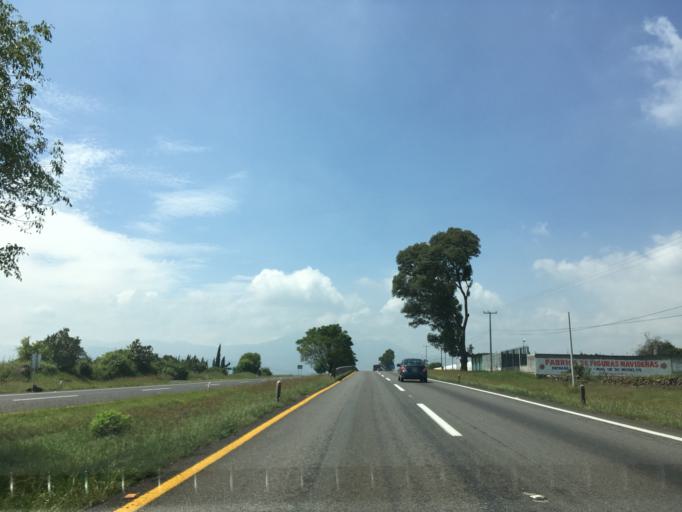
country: MX
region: Michoacan
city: Acuitzio del Canje
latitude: 19.5704
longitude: -101.3202
